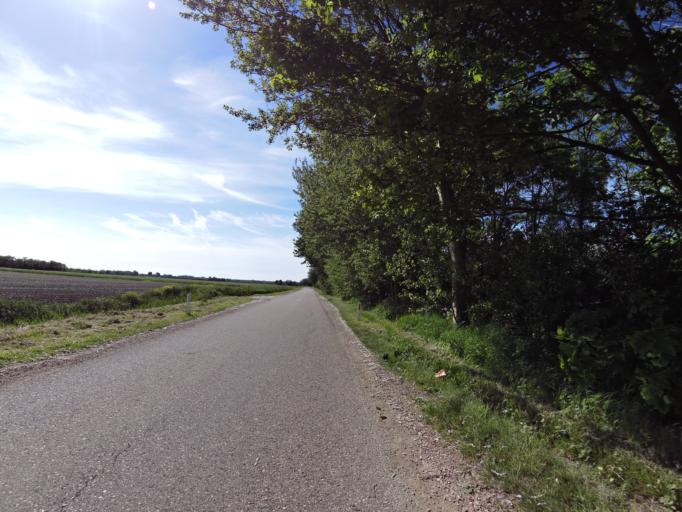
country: NL
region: South Holland
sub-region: Gemeente Brielle
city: Brielle
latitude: 51.8921
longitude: 4.1244
